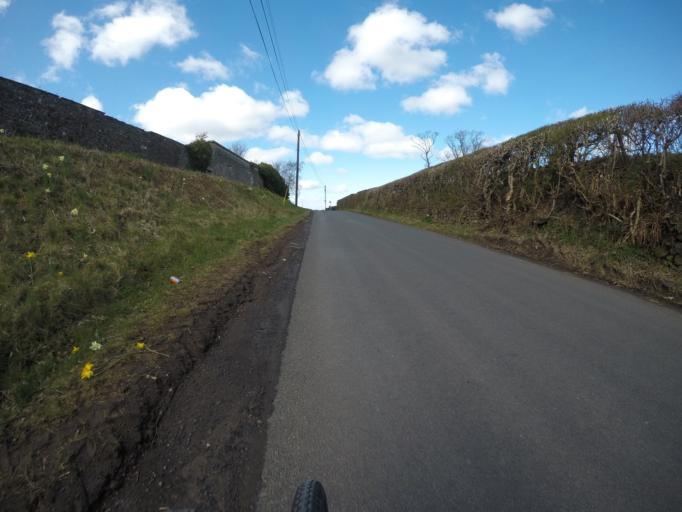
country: GB
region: Scotland
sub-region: East Ayrshire
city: Crosshouse
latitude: 55.6029
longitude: -4.5709
